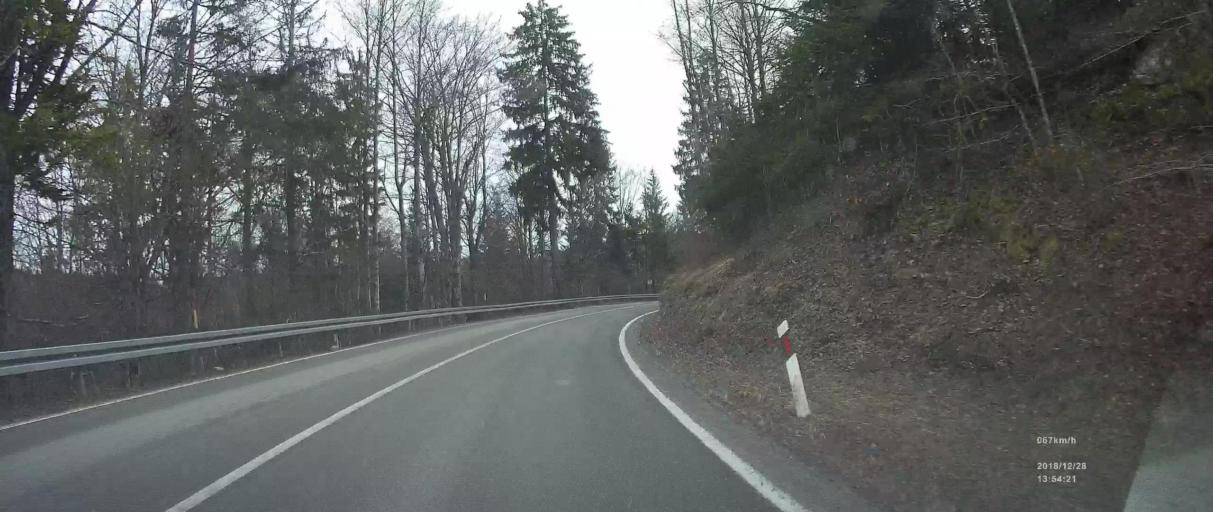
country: HR
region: Primorsko-Goranska
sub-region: Grad Delnice
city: Delnice
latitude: 45.3869
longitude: 14.8630
